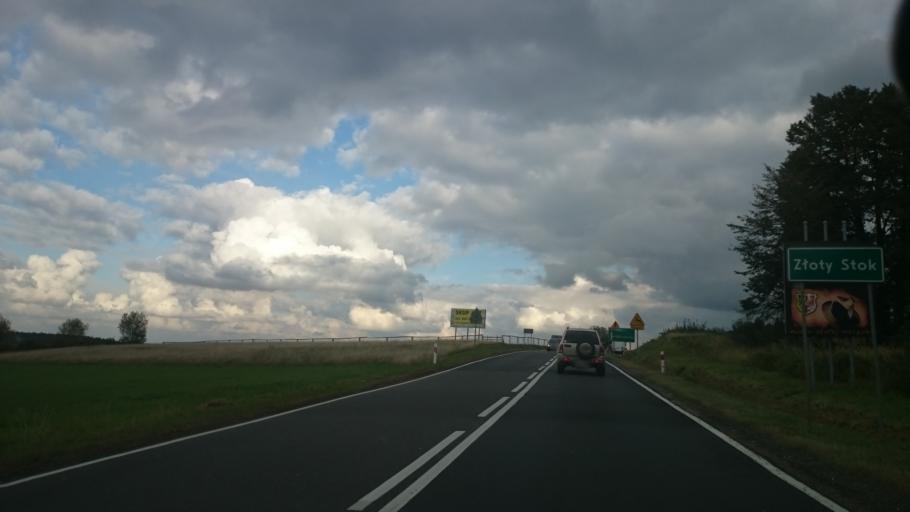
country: PL
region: Lower Silesian Voivodeship
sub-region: Powiat zabkowicki
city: Zloty Stok
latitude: 50.4470
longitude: 16.8629
